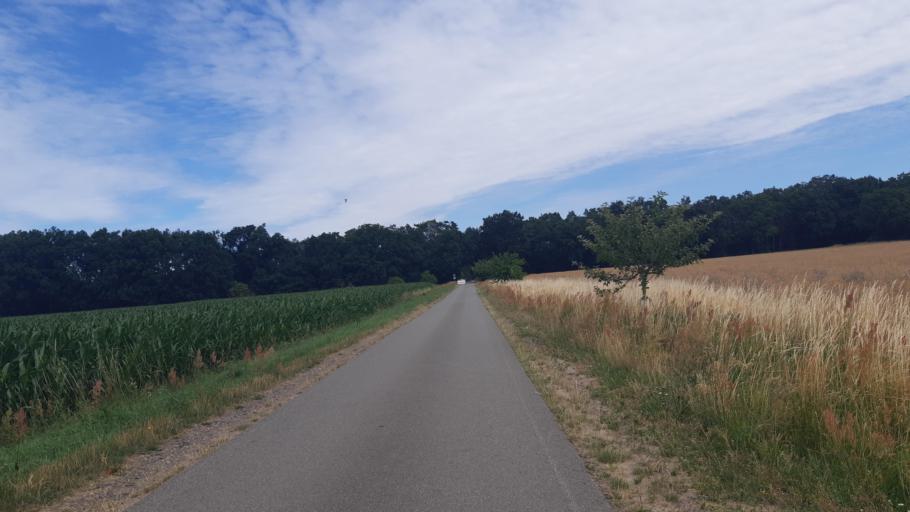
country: DE
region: Lower Saxony
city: Dahlem
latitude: 53.2351
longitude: 10.7794
